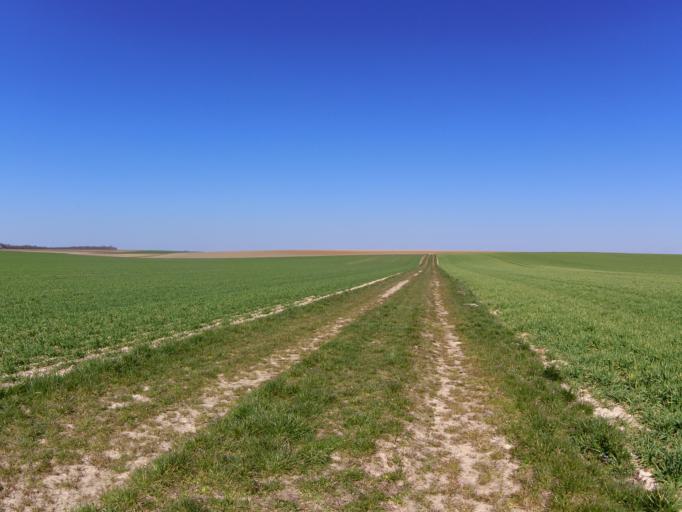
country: DE
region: Bavaria
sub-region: Regierungsbezirk Unterfranken
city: Oberpleichfeld
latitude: 49.8393
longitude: 10.0861
